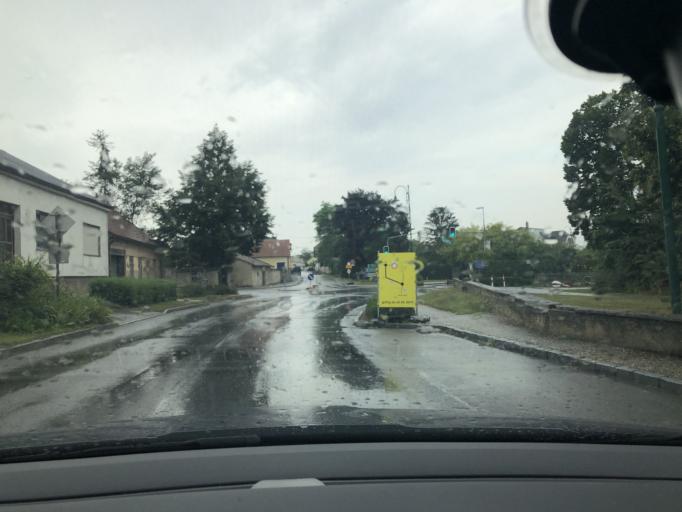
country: AT
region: Lower Austria
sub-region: Politischer Bezirk Ganserndorf
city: Ganserndorf
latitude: 48.3687
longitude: 16.6908
